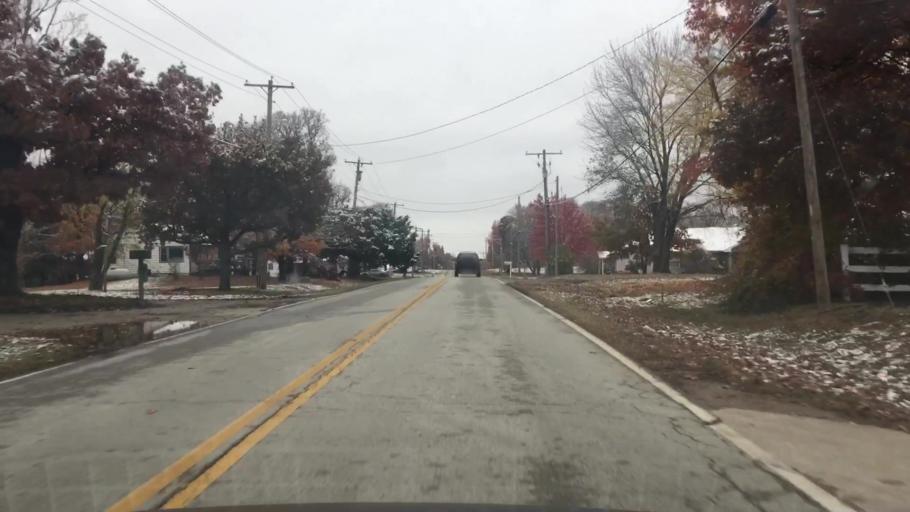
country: US
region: Missouri
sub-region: Saint Clair County
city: Osceola
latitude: 38.0356
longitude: -93.7027
